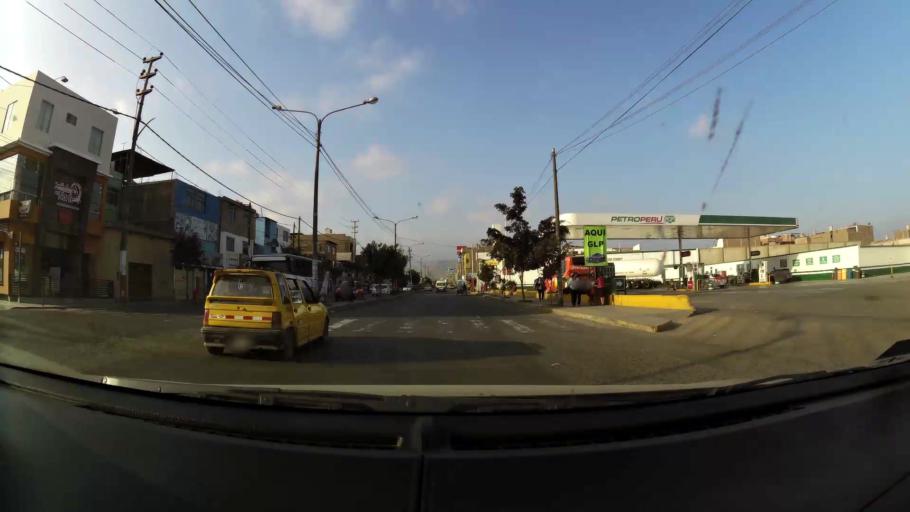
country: PE
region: La Libertad
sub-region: Provincia de Trujillo
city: El Porvenir
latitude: -8.0928
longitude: -79.0082
